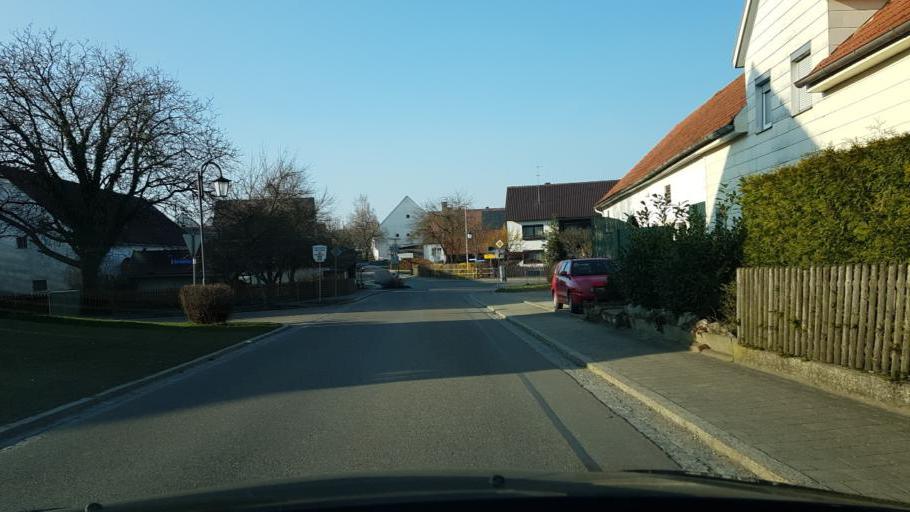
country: DE
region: Bavaria
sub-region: Upper Bavaria
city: Pfaffenhofen
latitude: 48.3691
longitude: 11.1928
